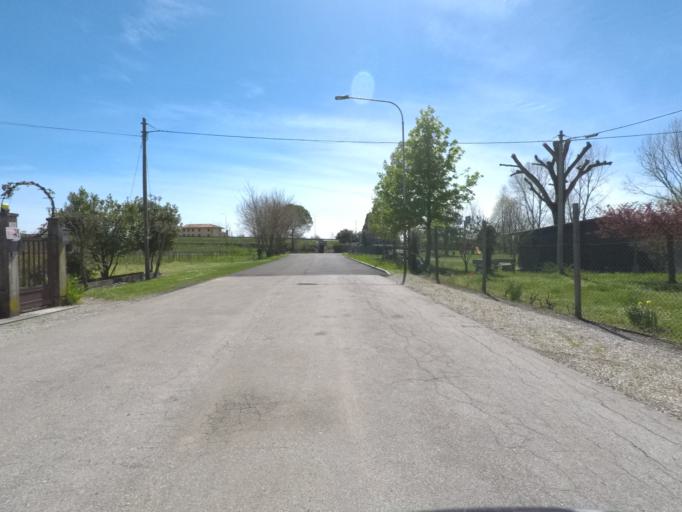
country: IT
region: Friuli Venezia Giulia
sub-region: Provincia di Pordenone
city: Valvasone
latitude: 45.9661
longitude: 12.8946
